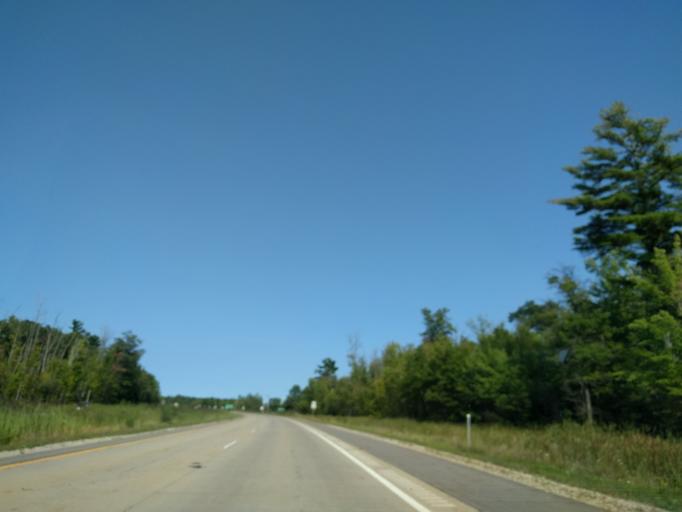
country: US
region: Wisconsin
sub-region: Oconto County
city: Oconto
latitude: 44.8145
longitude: -87.9490
